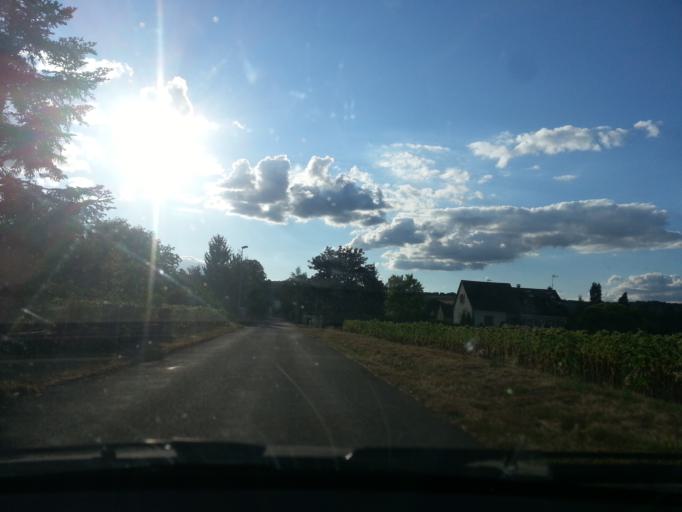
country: FR
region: Bourgogne
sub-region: Departement de Saone-et-Loire
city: Givry
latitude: 46.7786
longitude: 4.7531
